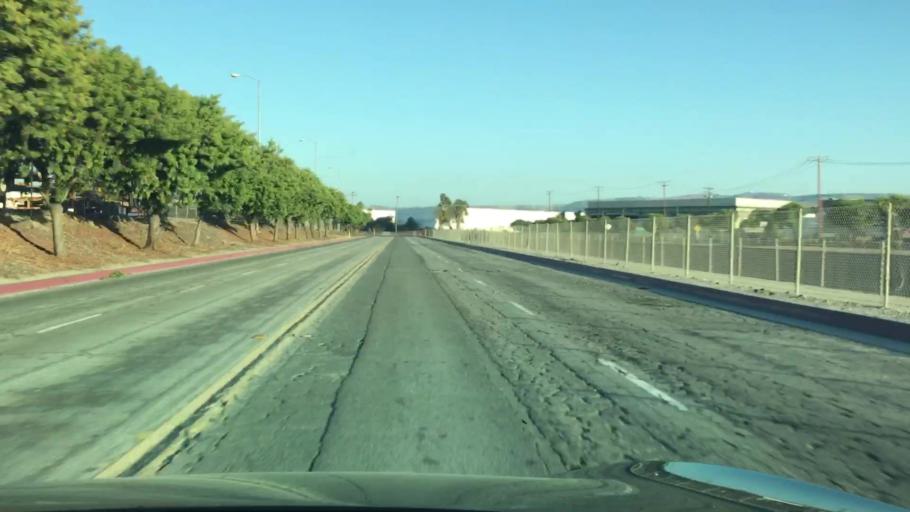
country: US
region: California
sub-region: Los Angeles County
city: South San Jose Hills
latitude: 34.0078
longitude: -117.9251
